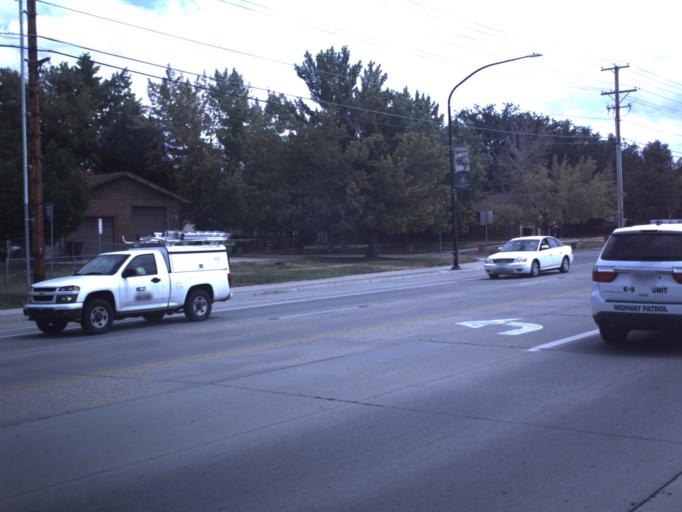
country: US
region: Utah
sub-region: Davis County
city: Syracuse
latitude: 41.0890
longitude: -112.0487
